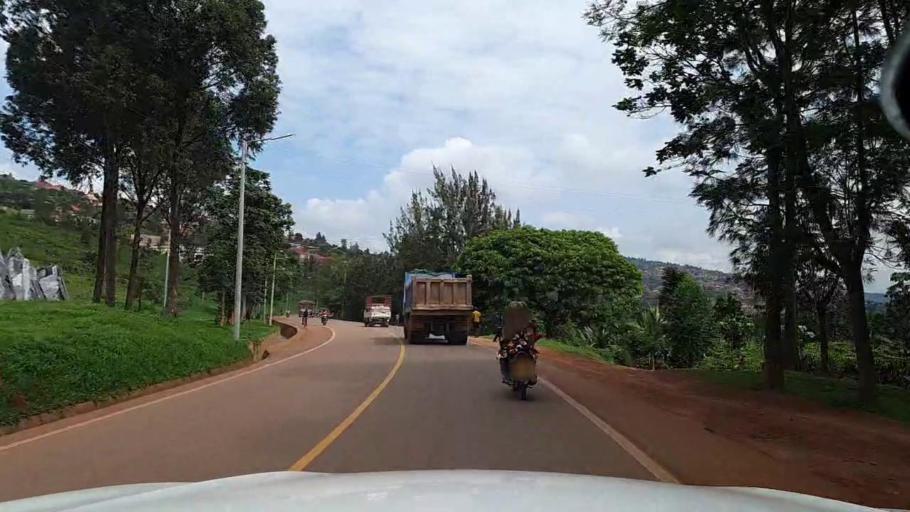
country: RW
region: Kigali
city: Kigali
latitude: -1.9135
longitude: 30.0480
